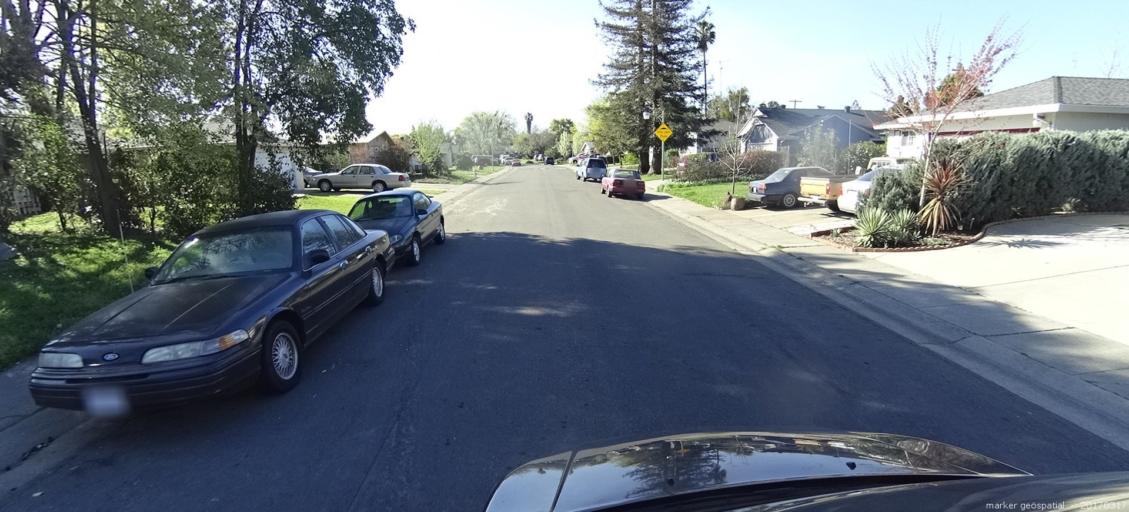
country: US
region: California
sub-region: Sacramento County
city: Parkway
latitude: 38.4942
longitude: -121.5002
